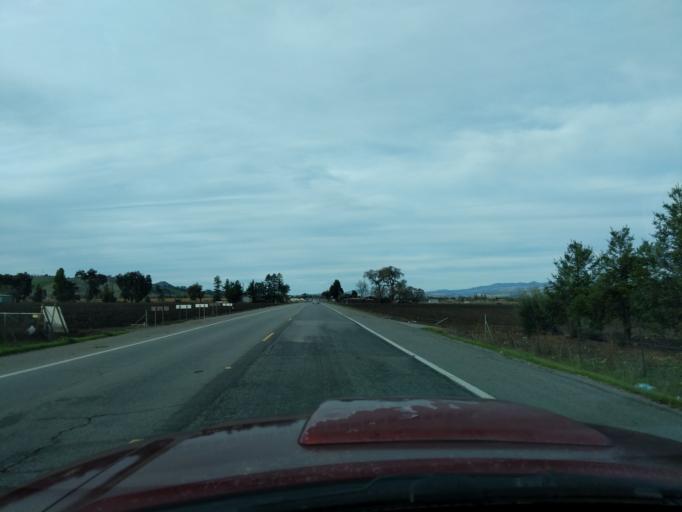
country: US
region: California
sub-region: Santa Clara County
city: San Martin
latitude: 37.0560
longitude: -121.6066
